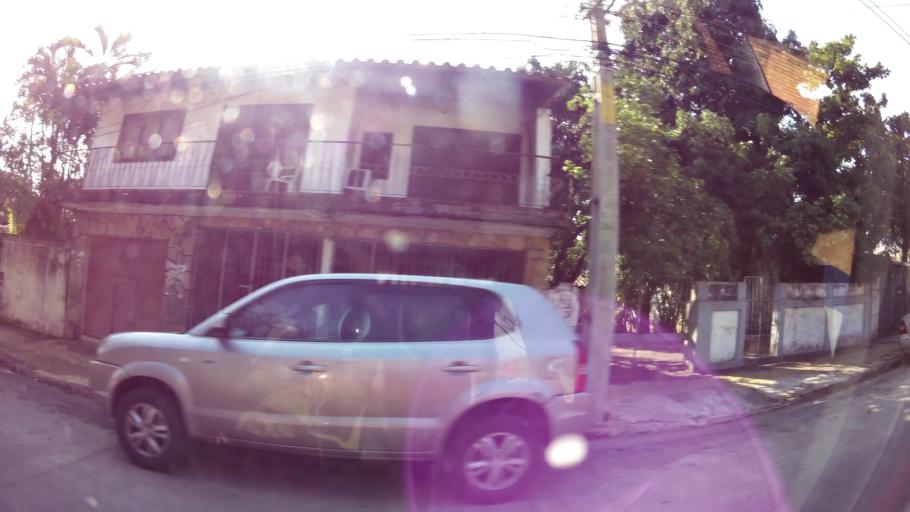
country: PY
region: Asuncion
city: Asuncion
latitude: -25.3146
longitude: -57.6284
